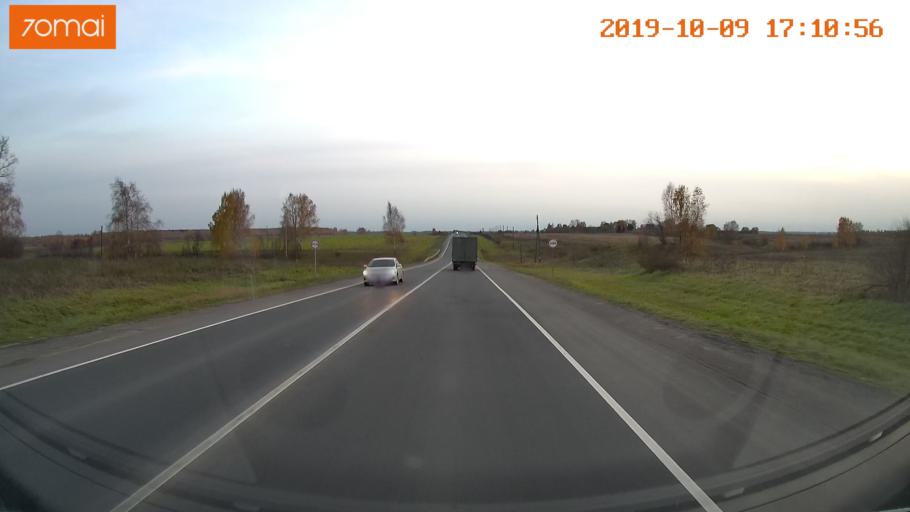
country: RU
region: Ivanovo
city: Privolzhsk
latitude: 57.3490
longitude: 41.2535
